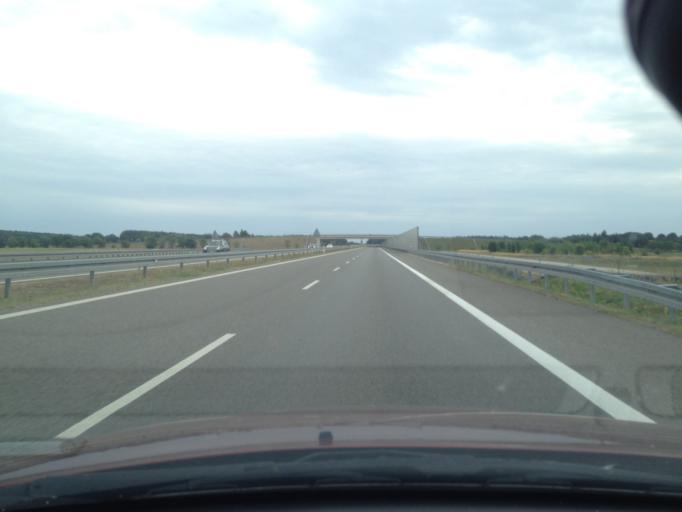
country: PL
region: West Pomeranian Voivodeship
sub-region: Powiat mysliborski
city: Nowogrodek Pomorski
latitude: 52.8859
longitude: 15.0231
